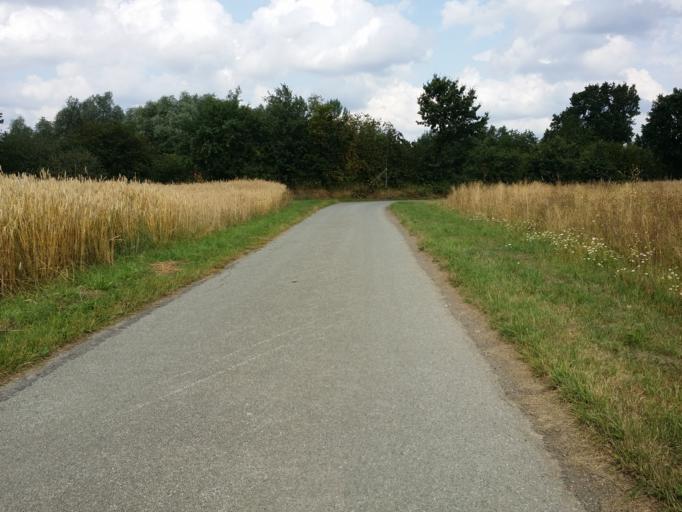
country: DE
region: Schleswig-Holstein
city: Mehlbek
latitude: 54.0005
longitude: 9.4261
